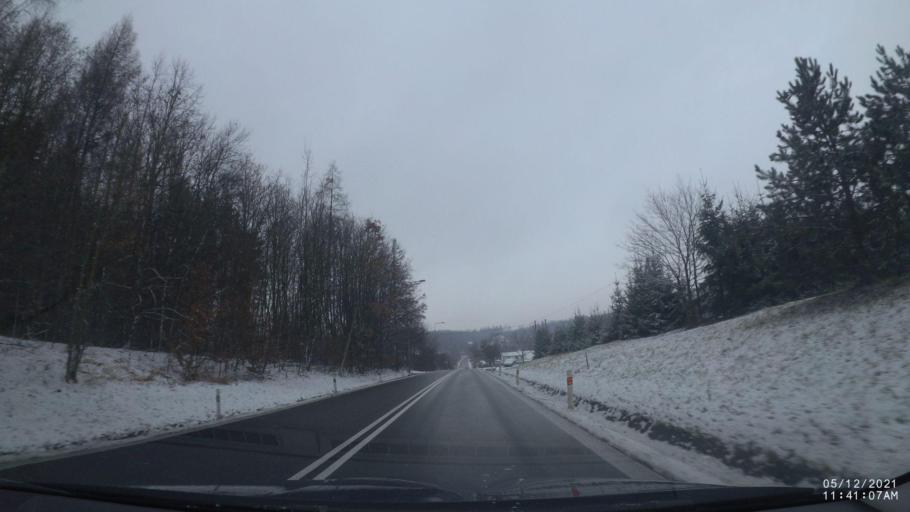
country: CZ
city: Dobruska
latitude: 50.2665
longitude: 16.1963
